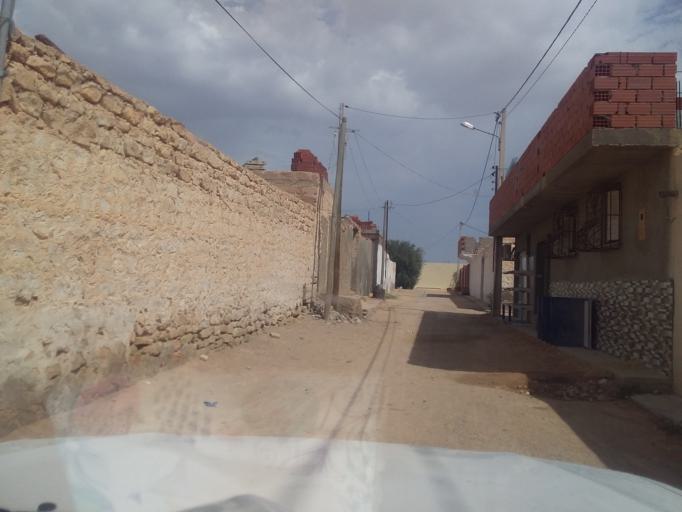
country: TN
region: Madanin
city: Medenine
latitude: 33.5853
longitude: 10.3235
